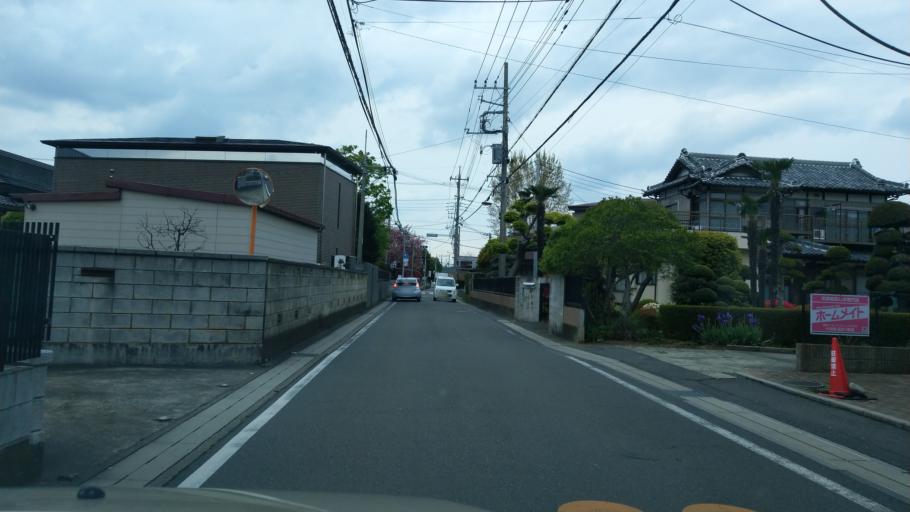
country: JP
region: Saitama
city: Yono
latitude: 35.9056
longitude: 139.5931
